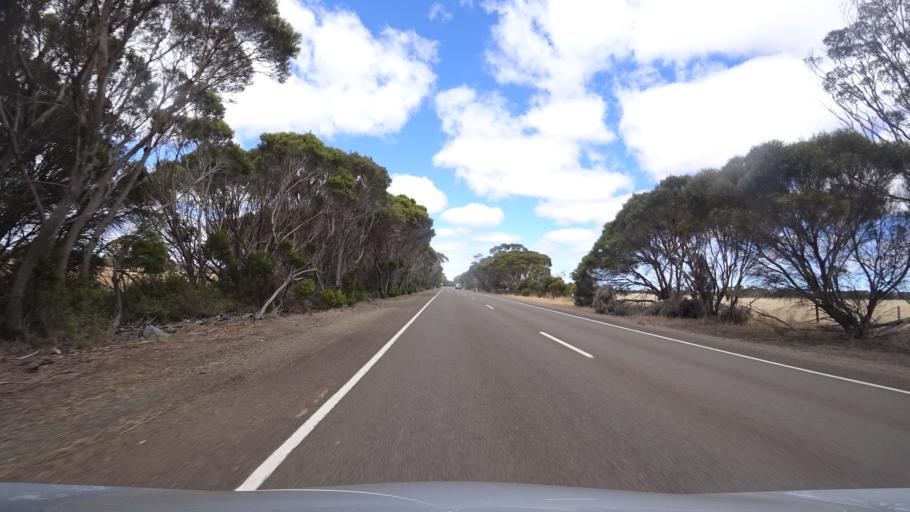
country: AU
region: South Australia
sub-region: Kangaroo Island
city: Kingscote
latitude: -35.6900
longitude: 137.5349
